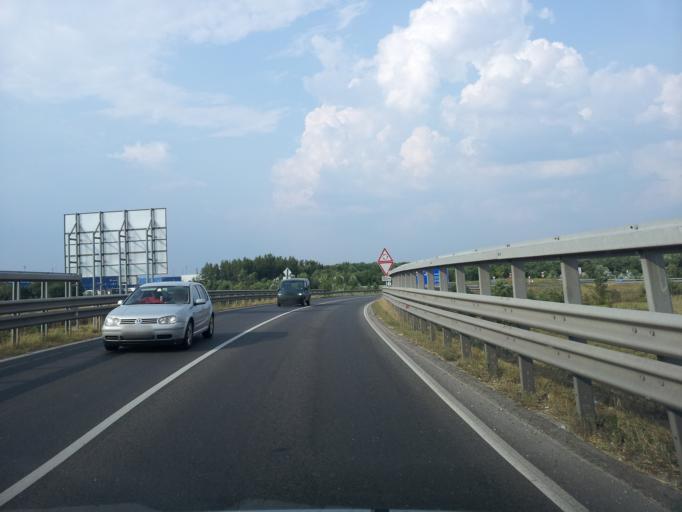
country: HU
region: Pest
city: Dunaharaszti
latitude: 47.3683
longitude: 19.1159
